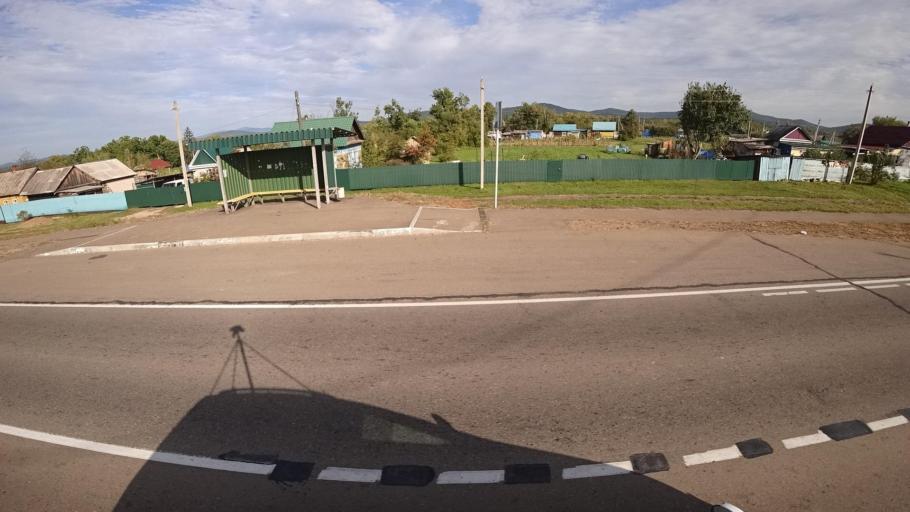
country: RU
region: Primorskiy
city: Dostoyevka
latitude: 44.3016
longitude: 133.4490
